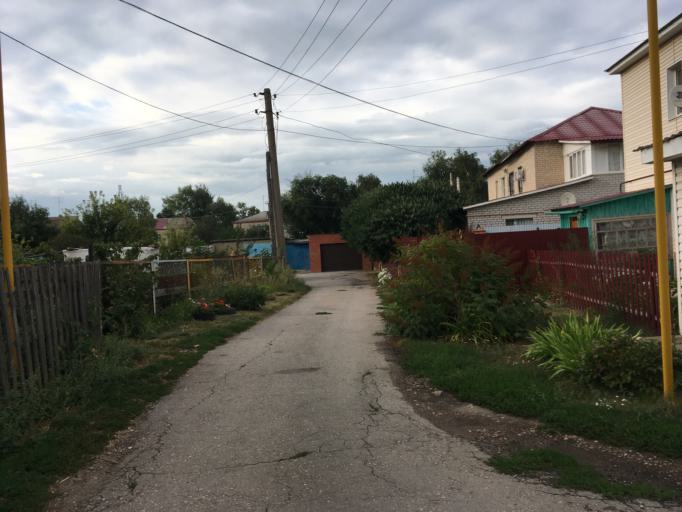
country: RU
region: Samara
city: Bezenchuk
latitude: 52.9867
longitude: 49.4434
